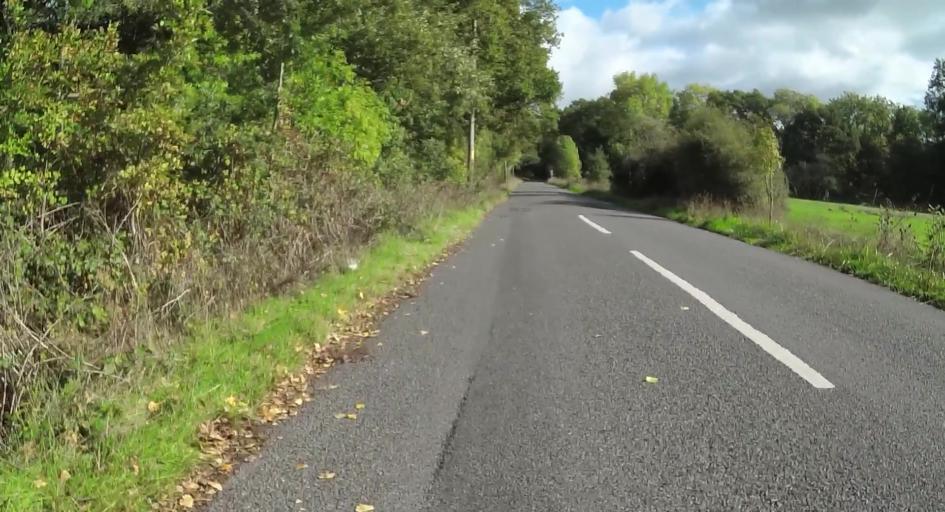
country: GB
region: England
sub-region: Hampshire
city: Odiham
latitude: 51.2654
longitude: -0.9274
